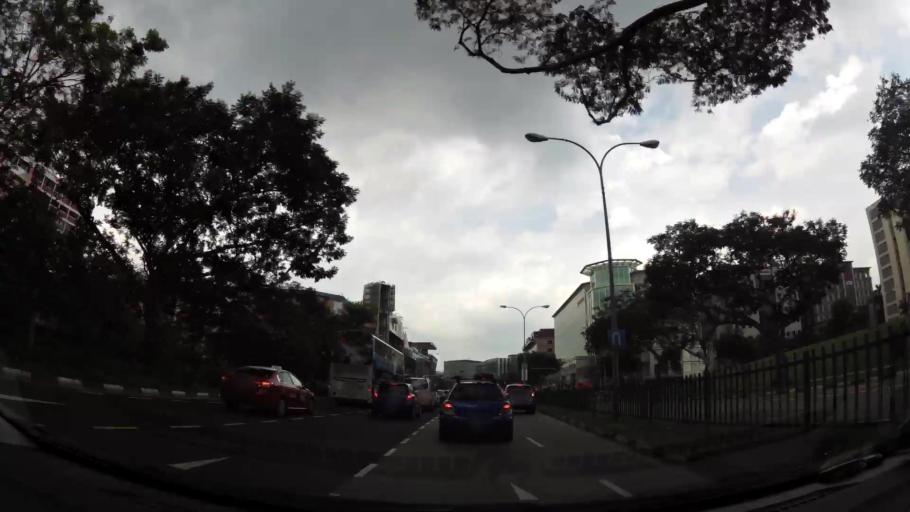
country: SG
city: Singapore
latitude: 1.3510
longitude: 103.9414
